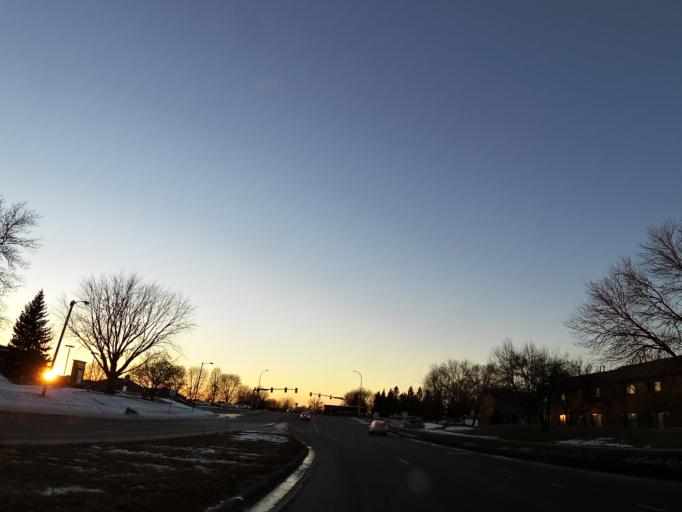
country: US
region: Minnesota
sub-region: Scott County
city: Savage
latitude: 44.8259
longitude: -93.3486
